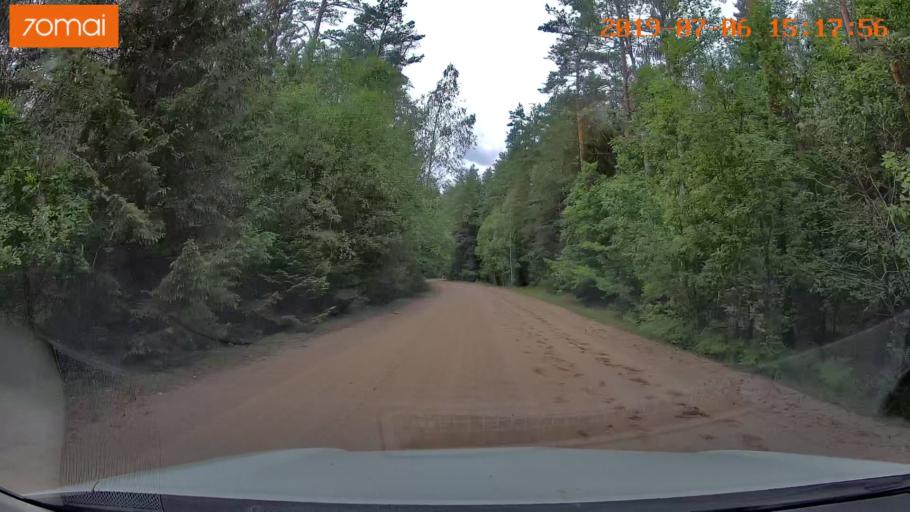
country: BY
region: Minsk
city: Ivyanyets
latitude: 53.9909
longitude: 26.6580
